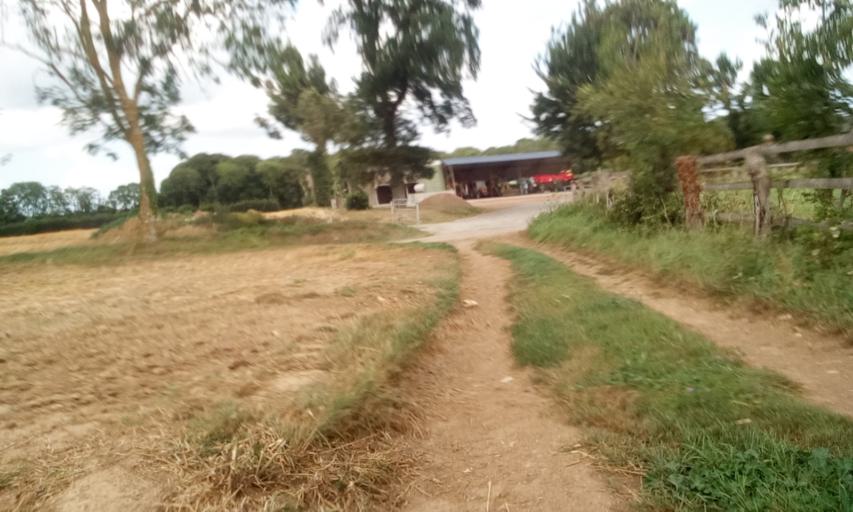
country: FR
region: Lower Normandy
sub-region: Departement du Calvados
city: Creully
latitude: 49.3106
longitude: -0.5545
